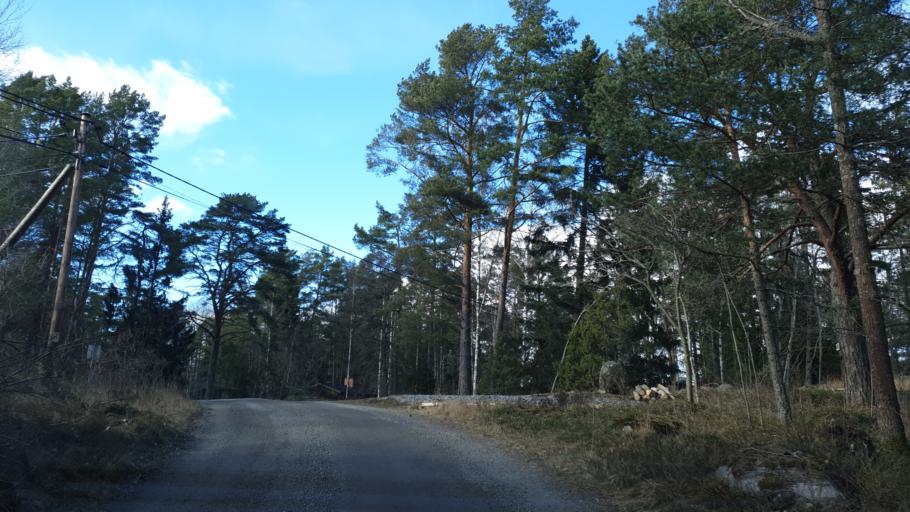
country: SE
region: Stockholm
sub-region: Varmdo Kommun
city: Holo
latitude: 59.2748
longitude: 18.6360
